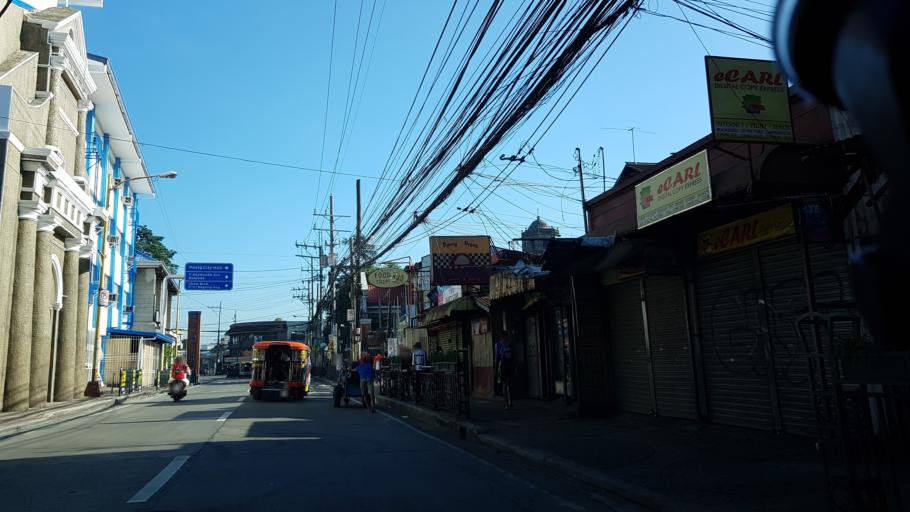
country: PH
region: Calabarzon
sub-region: Province of Rizal
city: Pateros
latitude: 14.5595
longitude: 121.0764
